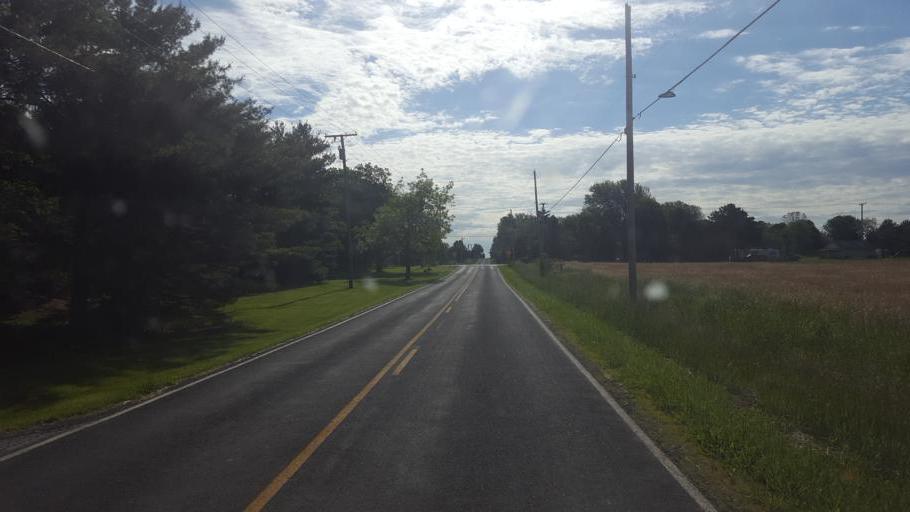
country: US
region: Ohio
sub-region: Medina County
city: Seville
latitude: 41.0471
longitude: -81.8338
